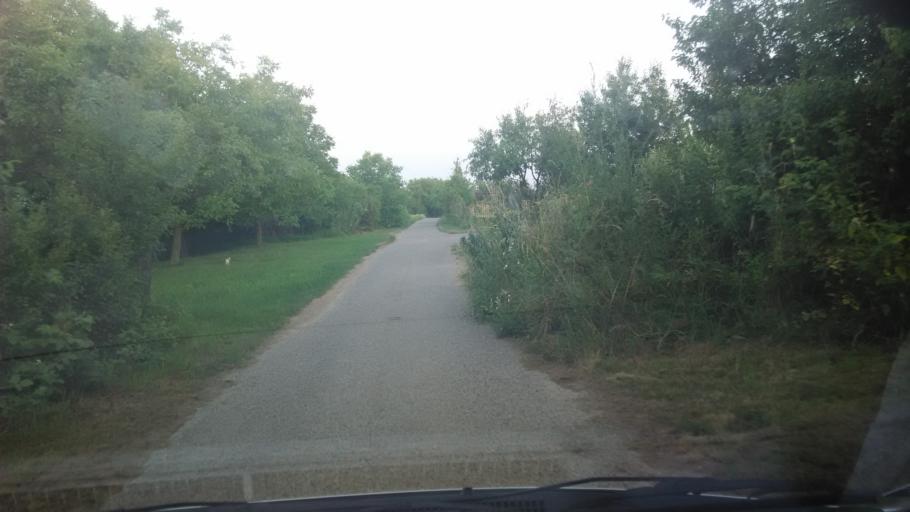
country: SK
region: Nitriansky
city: Levice
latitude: 48.1148
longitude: 18.4594
